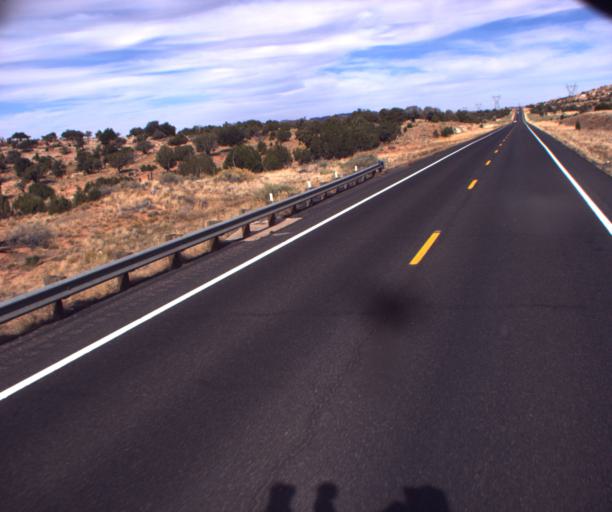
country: US
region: Arizona
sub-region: Navajo County
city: Kayenta
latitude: 36.6863
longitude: -110.3764
